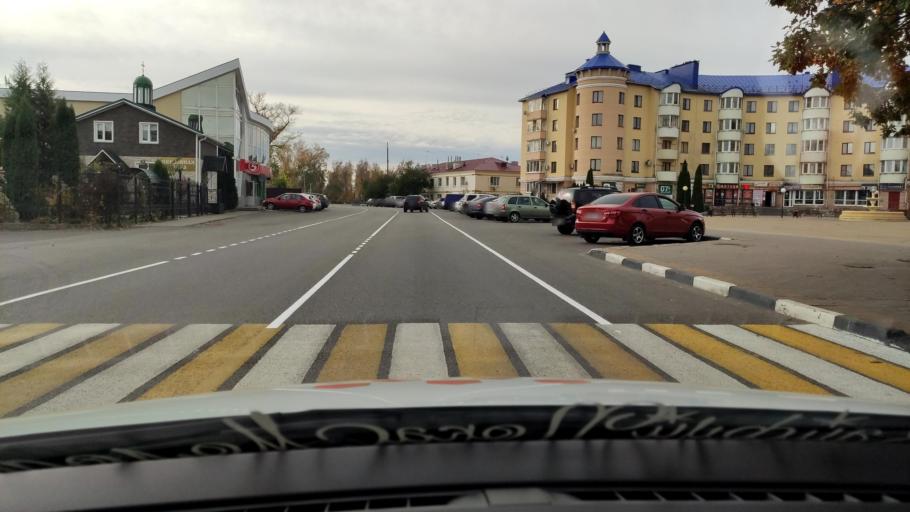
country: RU
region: Voronezj
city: Ramon'
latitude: 51.9129
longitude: 39.3390
